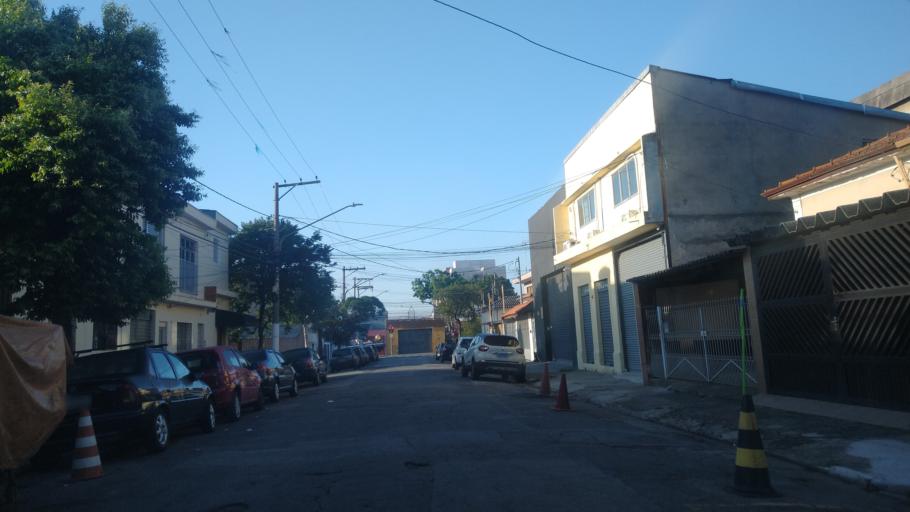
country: BR
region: Sao Paulo
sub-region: Sao Paulo
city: Sao Paulo
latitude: -23.5033
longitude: -46.6131
